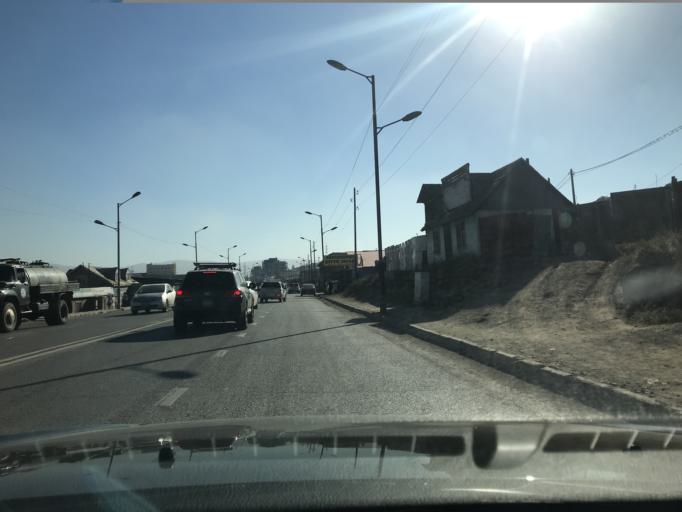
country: MN
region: Ulaanbaatar
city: Ulaanbaatar
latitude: 47.9736
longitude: 106.9179
